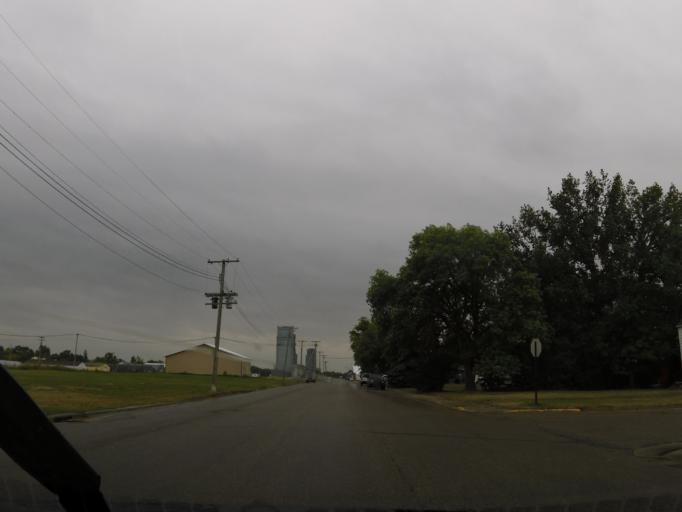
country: US
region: Minnesota
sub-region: Marshall County
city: Warren
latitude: 48.4544
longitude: -96.8757
